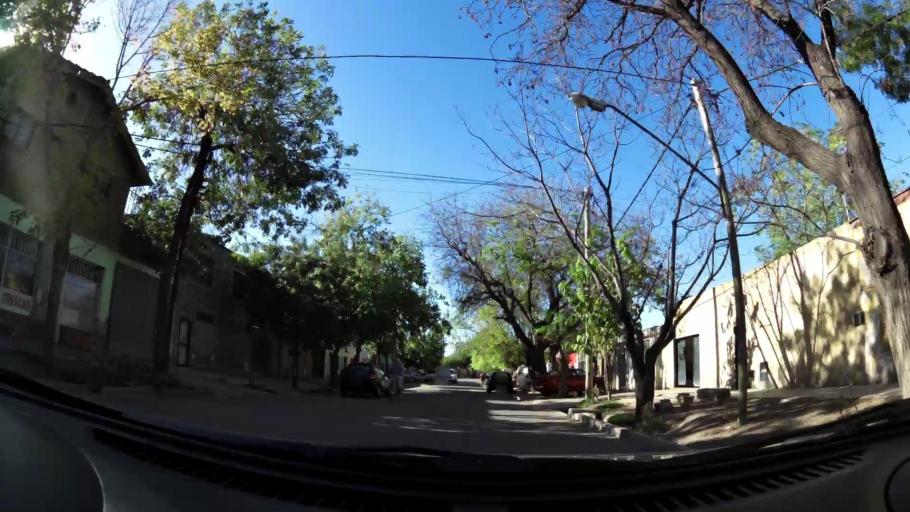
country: AR
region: Mendoza
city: Las Heras
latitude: -32.8420
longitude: -68.8145
